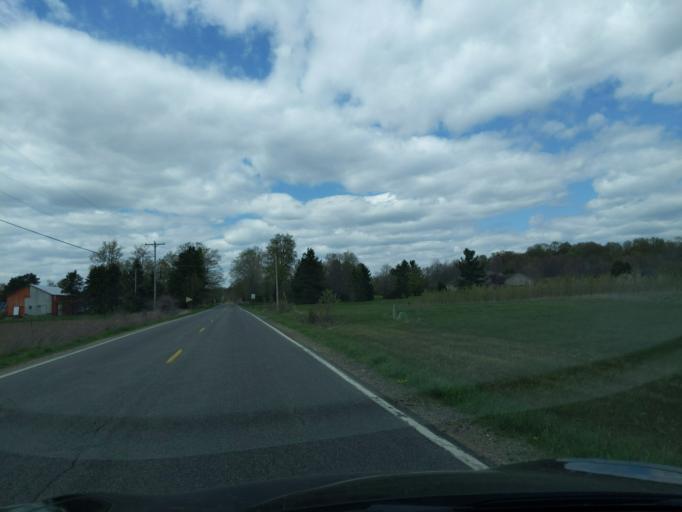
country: US
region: Michigan
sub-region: Ingham County
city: Mason
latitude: 42.6287
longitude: -84.4574
